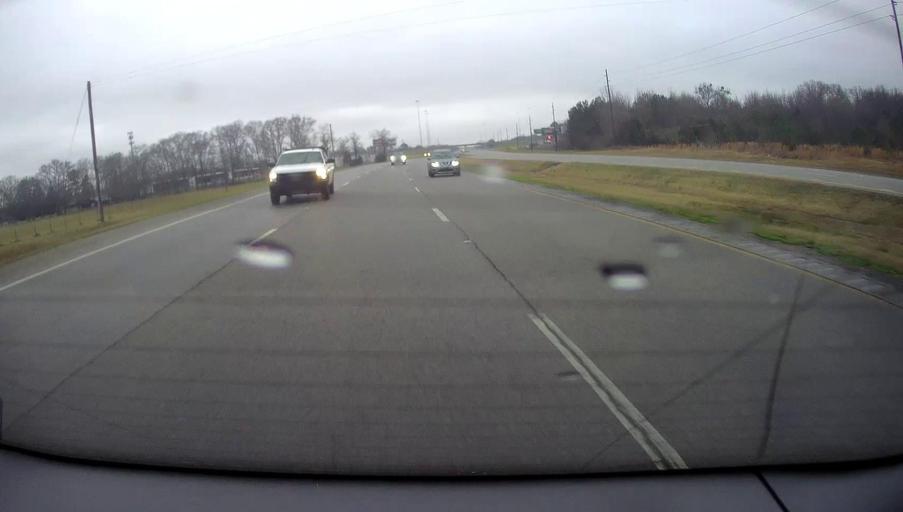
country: US
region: Alabama
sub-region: Morgan County
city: Decatur
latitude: 34.5946
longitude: -87.0313
